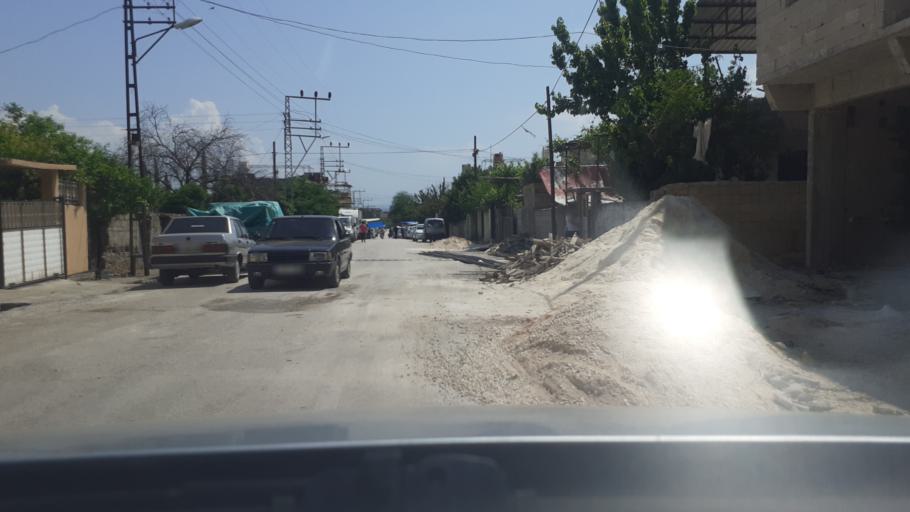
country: TR
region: Hatay
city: Kirikhan
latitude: 36.4933
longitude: 36.3540
